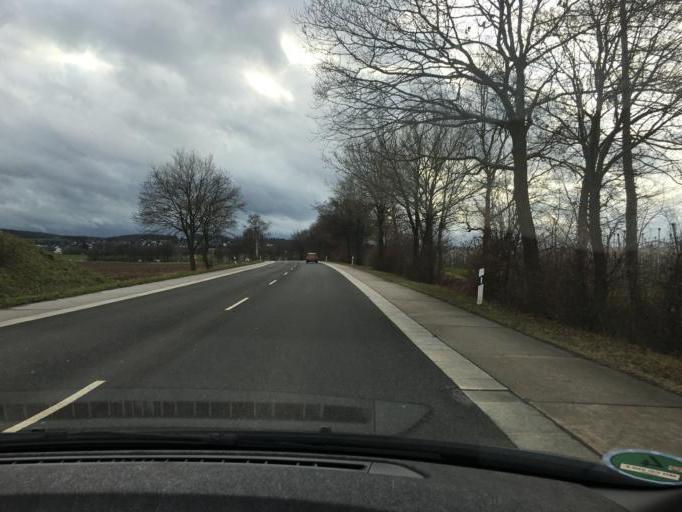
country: DE
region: North Rhine-Westphalia
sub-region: Regierungsbezirk Koln
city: Euskirchen
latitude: 50.6212
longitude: 6.8410
